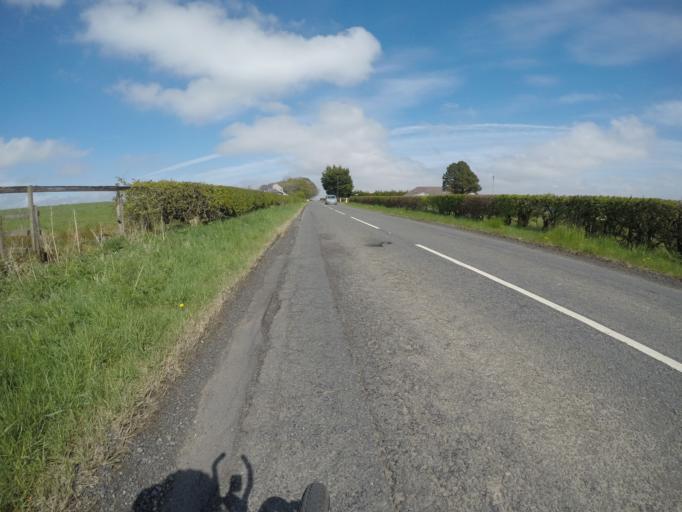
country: GB
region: Scotland
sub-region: East Ayrshire
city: Stewarton
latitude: 55.6974
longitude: -4.4869
